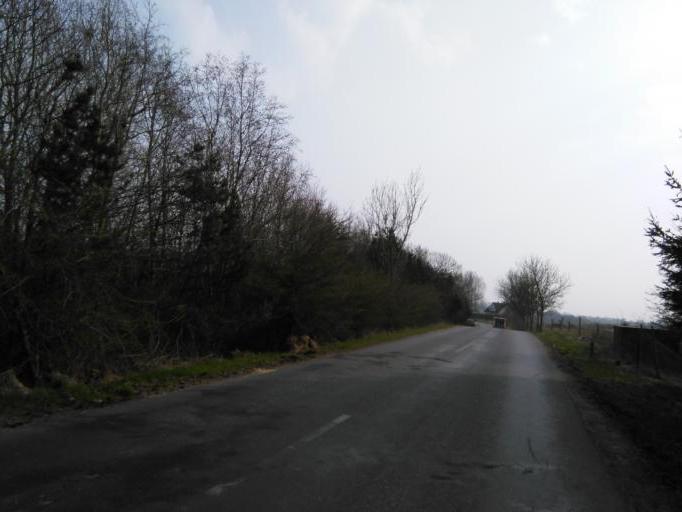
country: DK
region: Central Jutland
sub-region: Arhus Kommune
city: Beder
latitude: 56.0549
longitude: 10.2418
